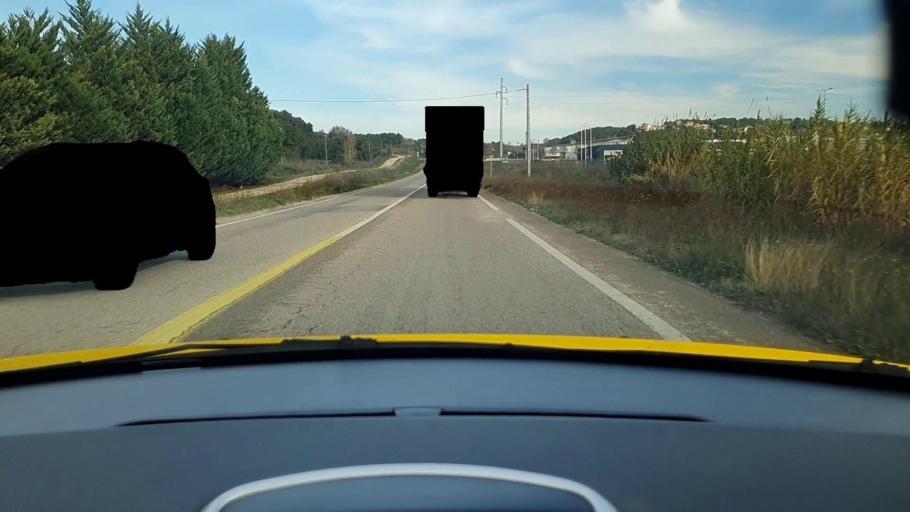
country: FR
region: Languedoc-Roussillon
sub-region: Departement du Gard
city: Beaucaire
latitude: 43.8111
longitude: 4.6109
